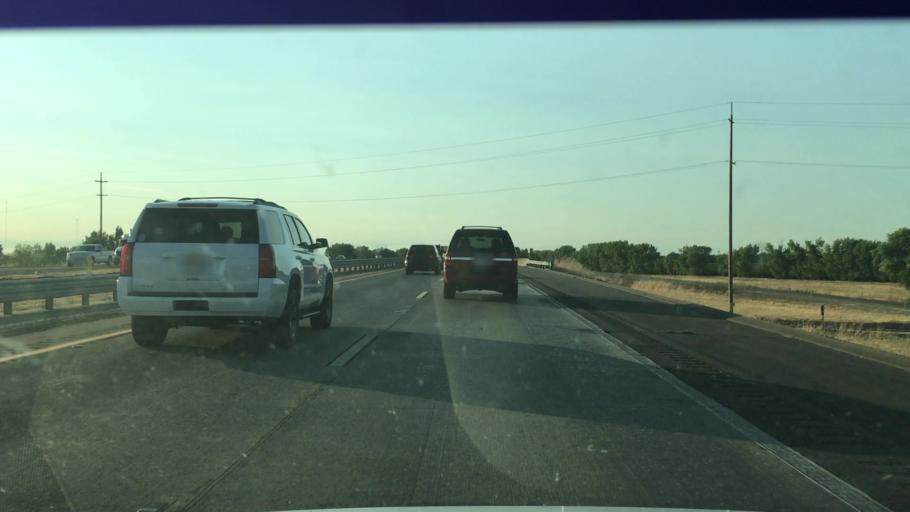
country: US
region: California
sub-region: San Joaquin County
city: Thornton
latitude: 38.1888
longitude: -121.4039
